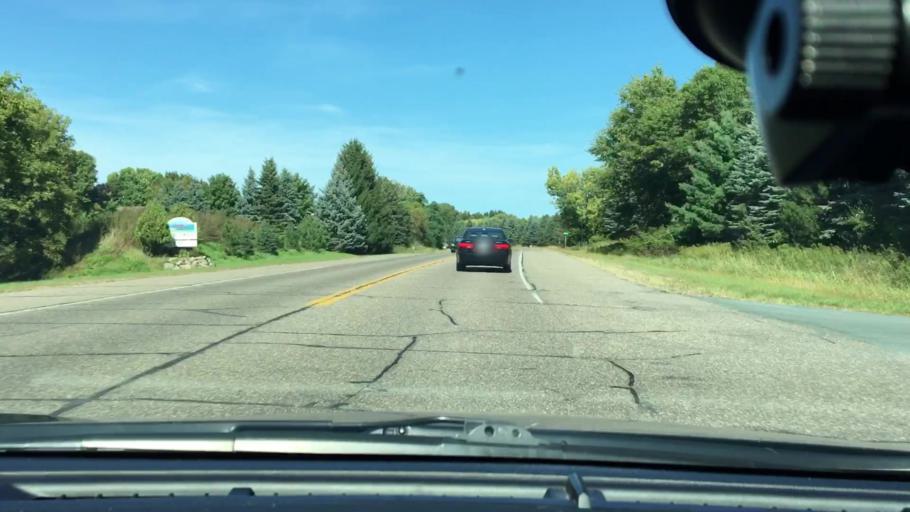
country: US
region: Minnesota
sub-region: Washington County
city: Mahtomedi
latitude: 45.0474
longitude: -92.9495
